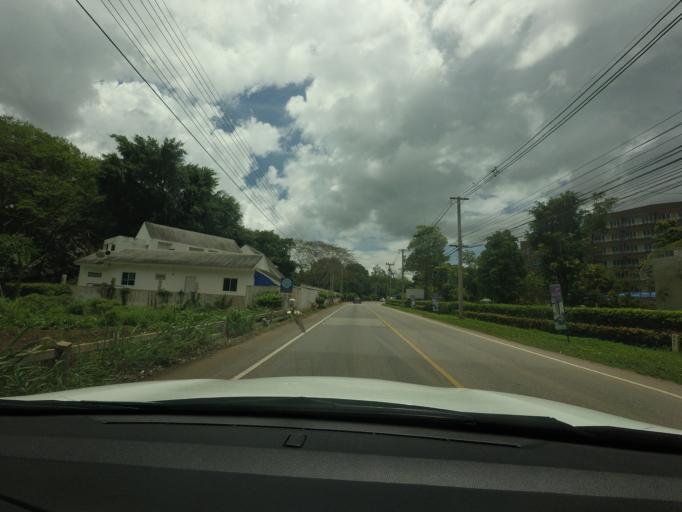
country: TH
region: Sara Buri
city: Muak Lek
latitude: 14.5414
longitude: 101.3397
